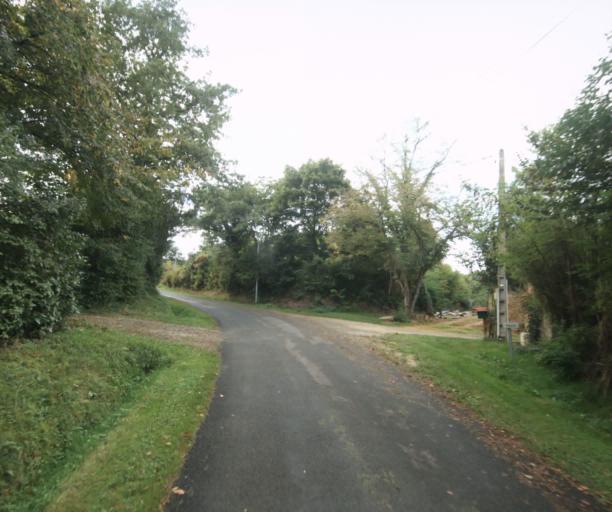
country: FR
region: Midi-Pyrenees
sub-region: Departement du Gers
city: Cazaubon
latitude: 43.8711
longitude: -0.1116
